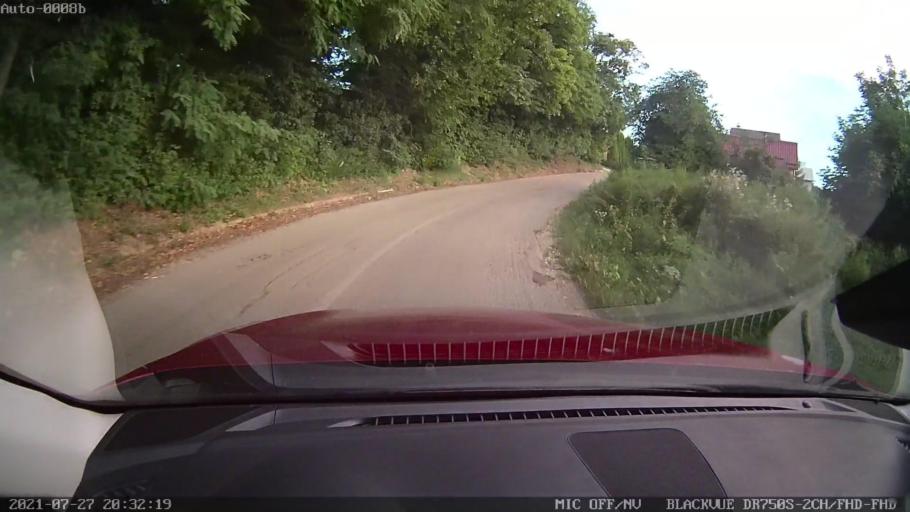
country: HR
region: Varazdinska
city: Jalzabet
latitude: 46.2433
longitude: 16.4758
